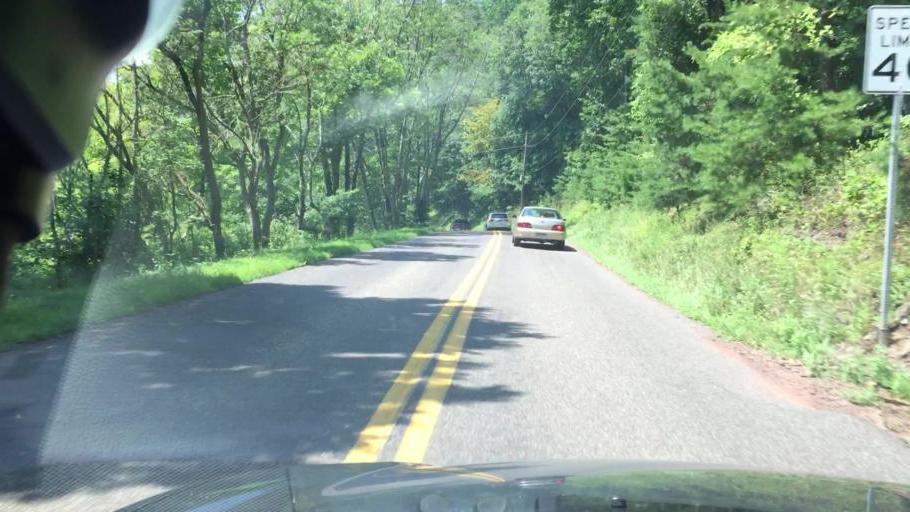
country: US
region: Pennsylvania
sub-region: Columbia County
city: Catawissa
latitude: 40.9616
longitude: -76.4393
